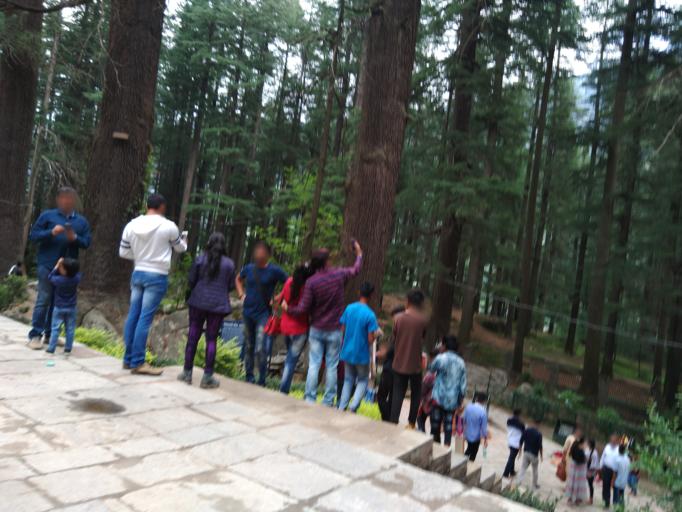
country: IN
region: Himachal Pradesh
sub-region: Kulu
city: Manali
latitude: 32.2483
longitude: 77.1809
